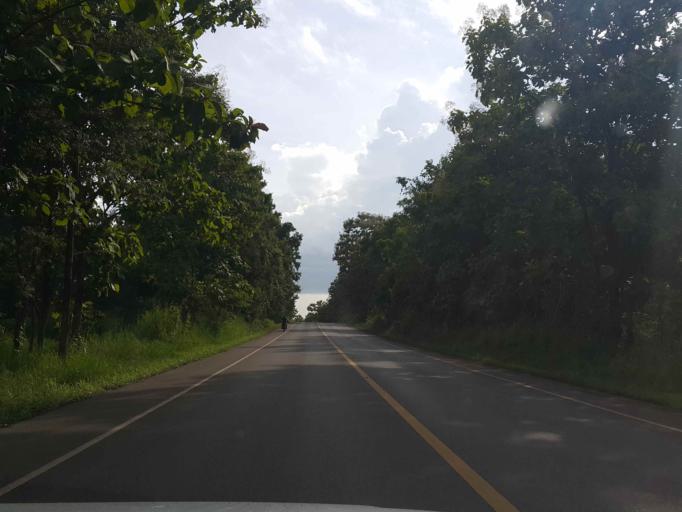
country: TH
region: Phrae
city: Den Chai
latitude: 17.8354
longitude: 99.8703
